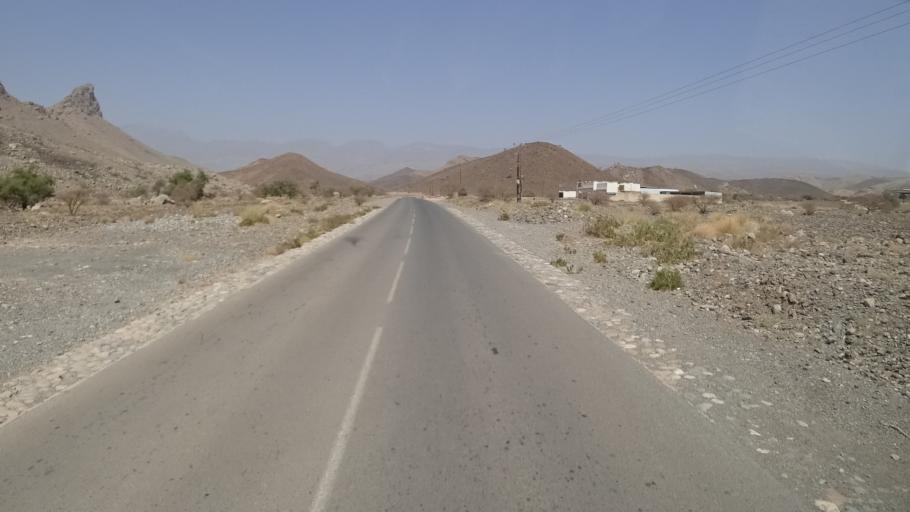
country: OM
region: Muhafazat ad Dakhiliyah
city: Bahla'
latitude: 23.0571
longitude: 57.3191
